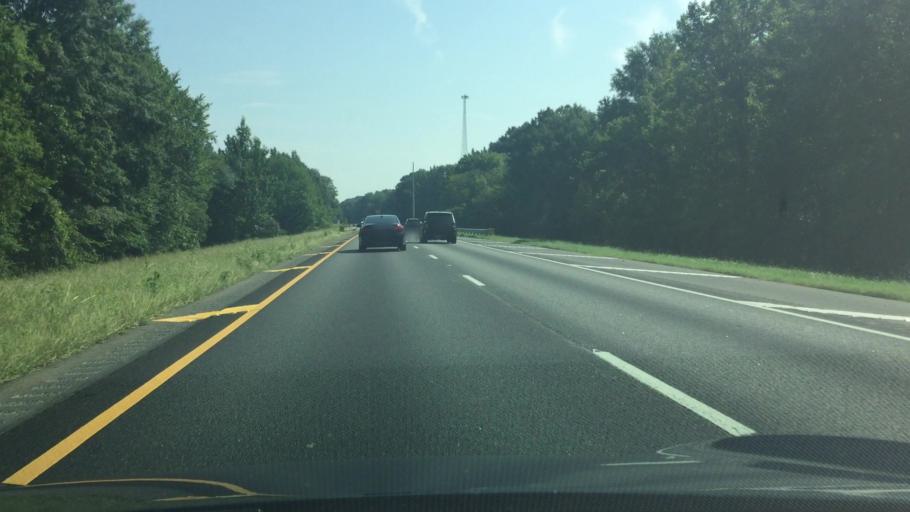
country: US
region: Alabama
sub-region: Montgomery County
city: Montgomery
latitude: 32.2287
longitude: -86.3868
